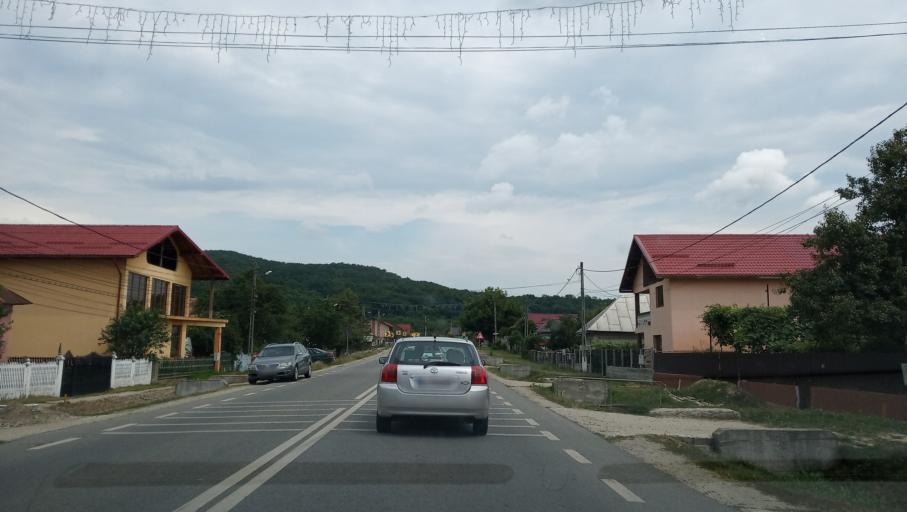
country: RO
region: Gorj
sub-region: Comuna Balteni
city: Pesteana Jiu
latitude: 44.8471
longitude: 23.3013
